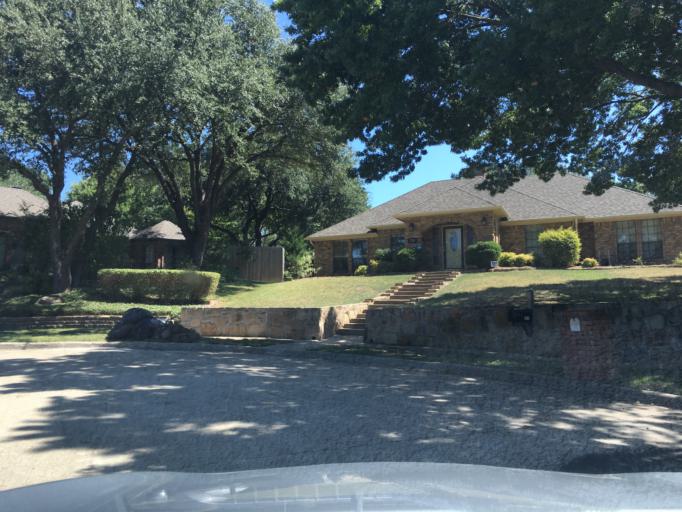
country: US
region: Texas
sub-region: Dallas County
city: Garland
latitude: 32.9515
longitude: -96.6316
